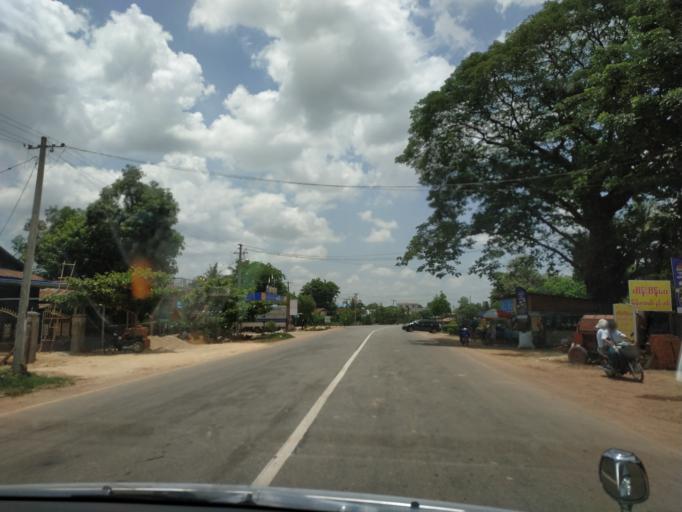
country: MM
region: Bago
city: Bago
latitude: 17.4736
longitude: 96.5373
